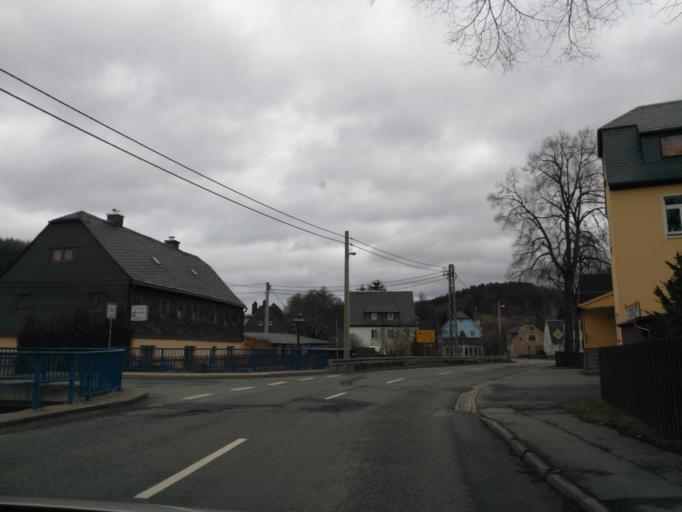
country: DE
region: Saxony
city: Thum
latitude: 50.6768
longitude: 12.9782
